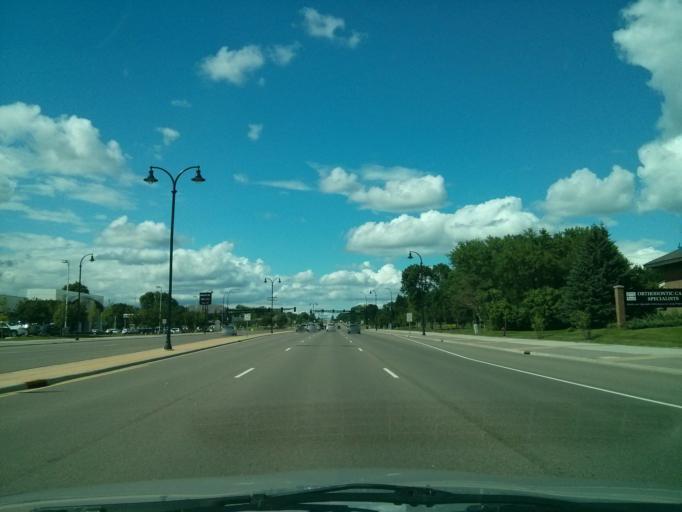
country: US
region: Minnesota
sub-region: Dakota County
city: Apple Valley
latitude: 44.7373
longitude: -93.2177
